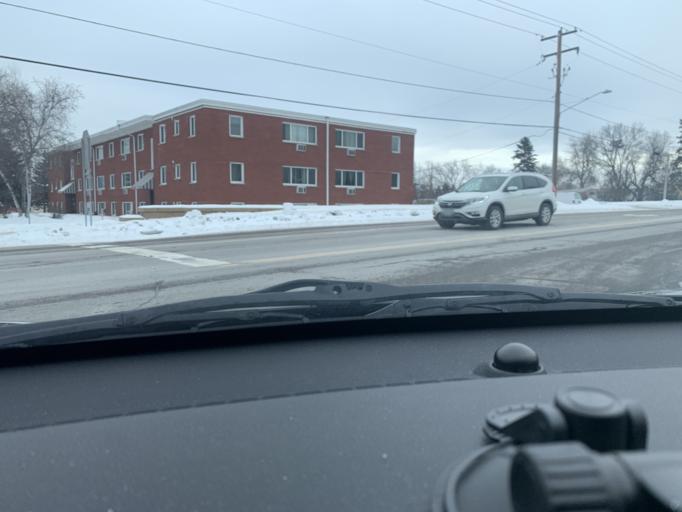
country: US
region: Minnesota
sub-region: Dakota County
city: South Saint Paul
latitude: 44.8902
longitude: -93.0705
